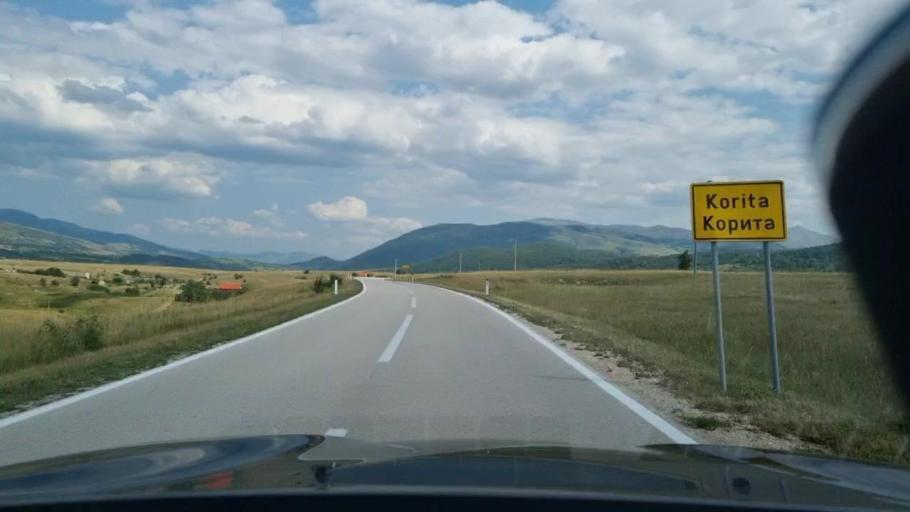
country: BA
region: Federation of Bosnia and Herzegovina
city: Bosansko Grahovo
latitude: 44.1554
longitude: 16.4338
